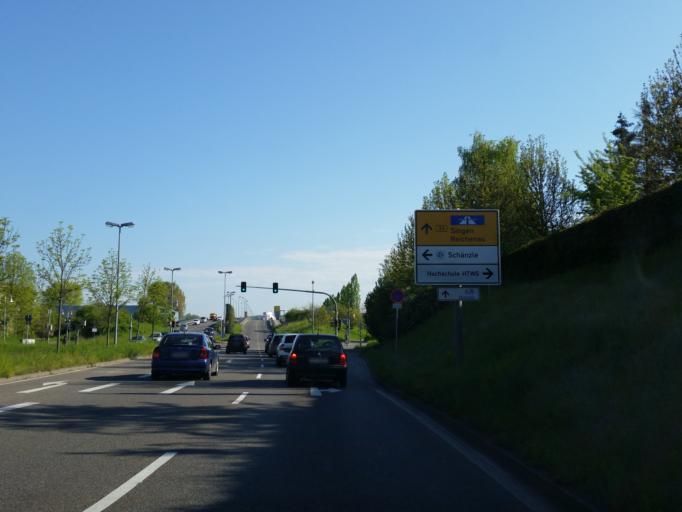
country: DE
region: Baden-Wuerttemberg
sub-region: Freiburg Region
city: Konstanz
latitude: 47.6657
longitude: 9.1622
